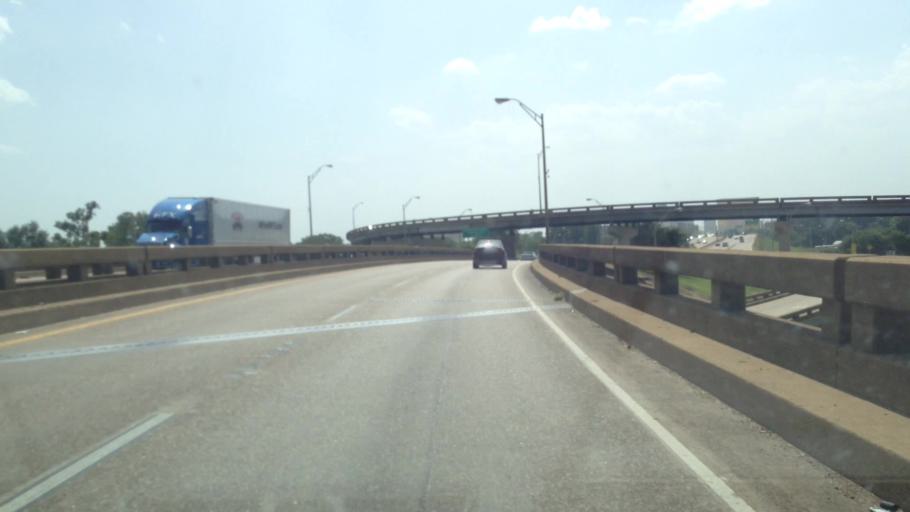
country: US
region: Louisiana
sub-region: Bossier Parish
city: Bossier City
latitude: 32.5134
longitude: -93.7148
